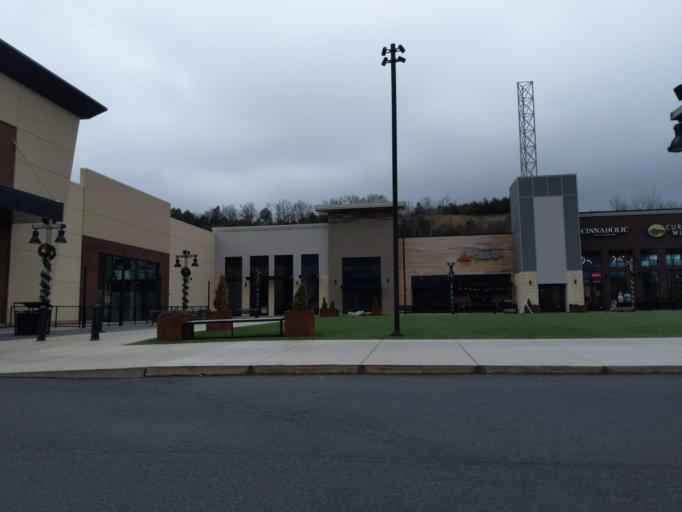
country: US
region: Tennessee
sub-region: Sevier County
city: Pigeon Forge
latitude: 35.8066
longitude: -83.5716
